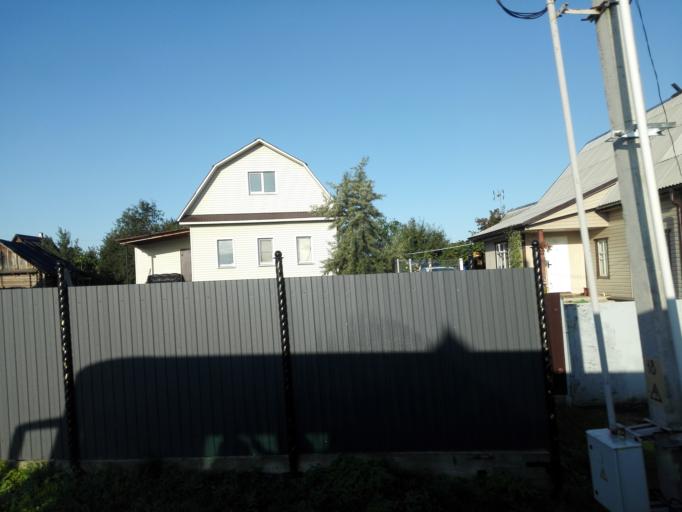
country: BY
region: Mogilev
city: Yalizava
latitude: 53.3260
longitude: 29.0501
